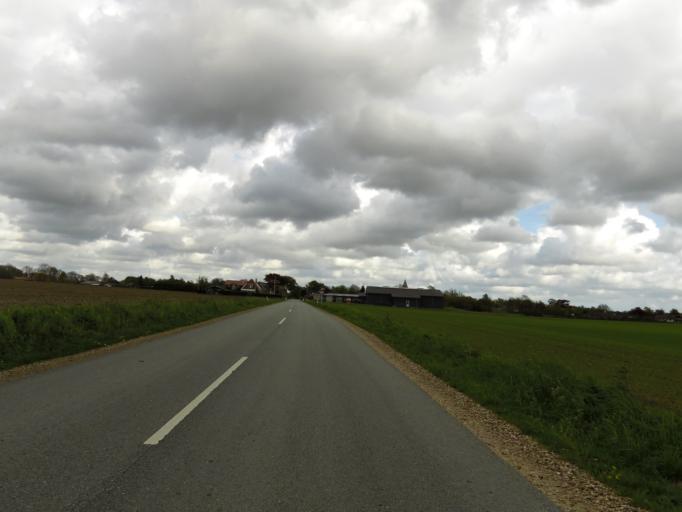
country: DK
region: South Denmark
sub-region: Haderslev Kommune
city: Gram
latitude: 55.3180
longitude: 8.9753
